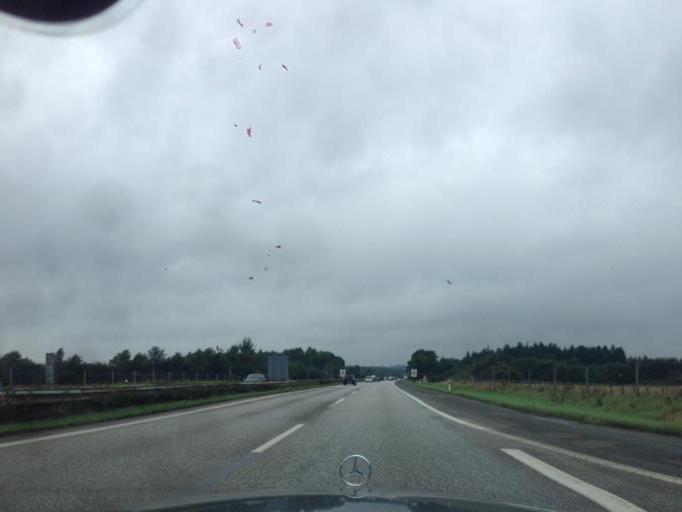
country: DE
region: Schleswig-Holstein
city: Bimohlen
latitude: 53.9086
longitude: 9.9367
